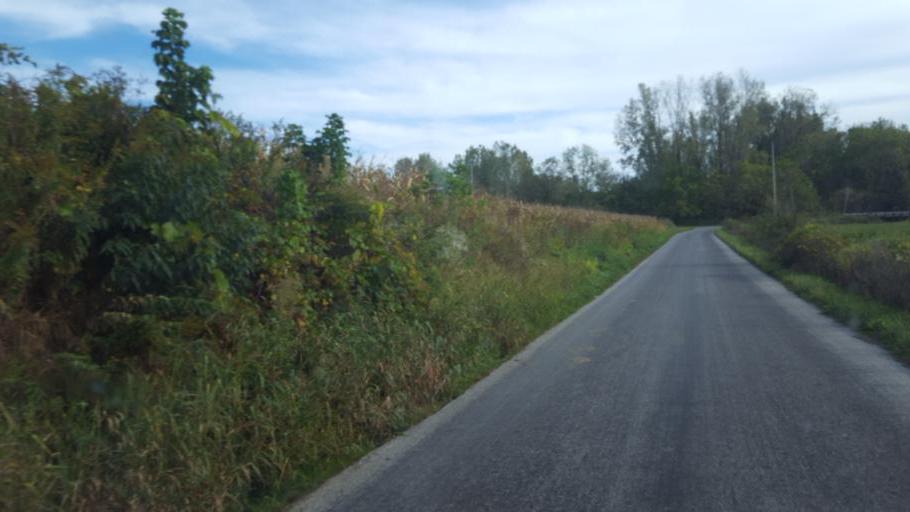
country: US
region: Ohio
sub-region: Knox County
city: Fredericktown
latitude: 40.5285
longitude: -82.5936
